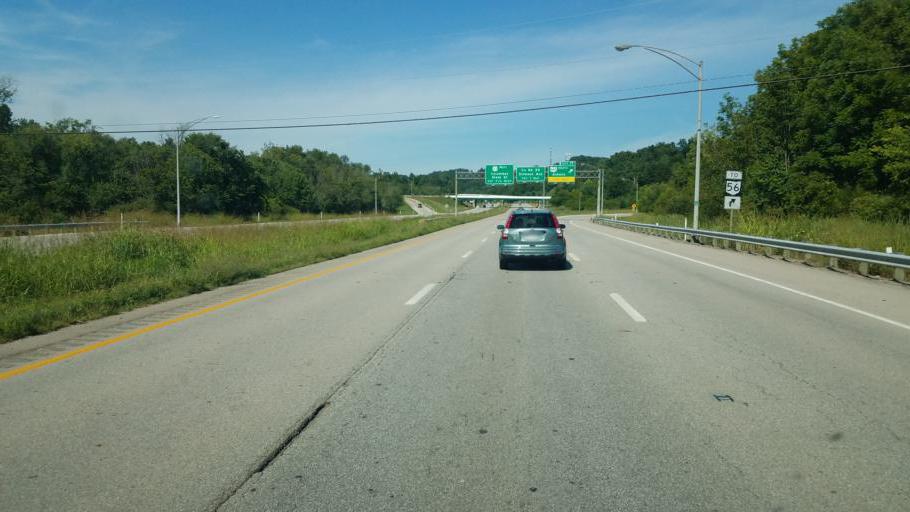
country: US
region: Ohio
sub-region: Athens County
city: Athens
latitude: 39.3118
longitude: -82.1028
